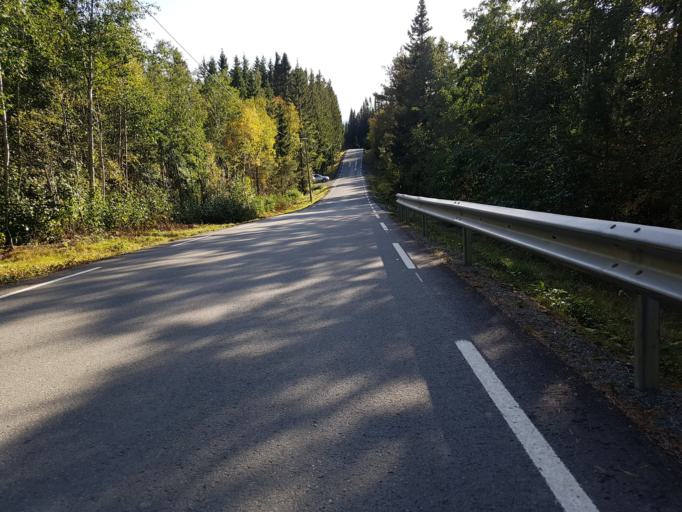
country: NO
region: Sor-Trondelag
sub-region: Malvik
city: Malvik
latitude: 63.3804
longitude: 10.6002
